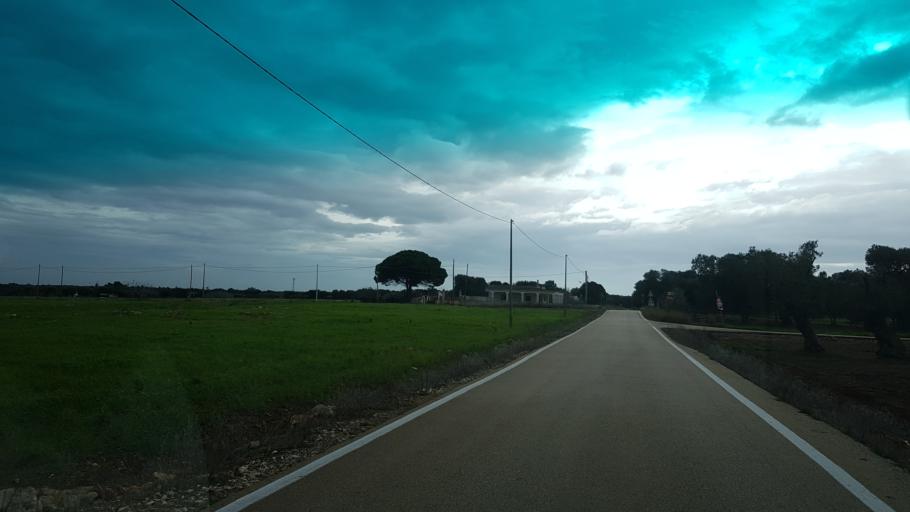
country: IT
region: Apulia
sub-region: Provincia di Brindisi
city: San Vito dei Normanni
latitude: 40.7110
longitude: 17.7662
